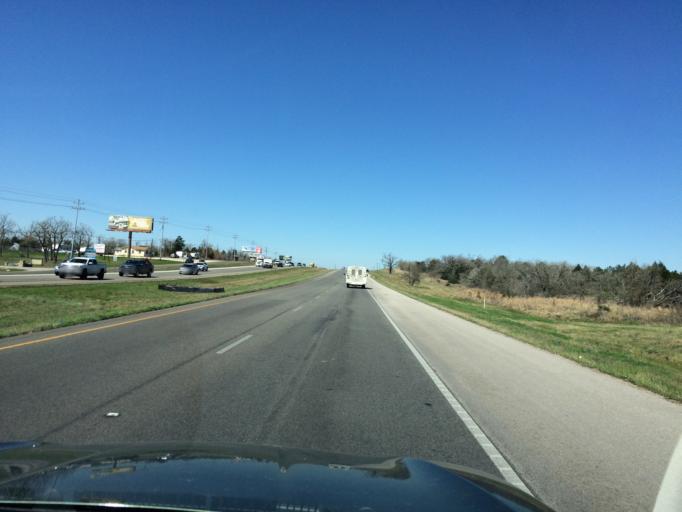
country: US
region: Texas
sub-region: Bastrop County
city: Wyldwood
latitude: 30.1302
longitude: -97.4464
